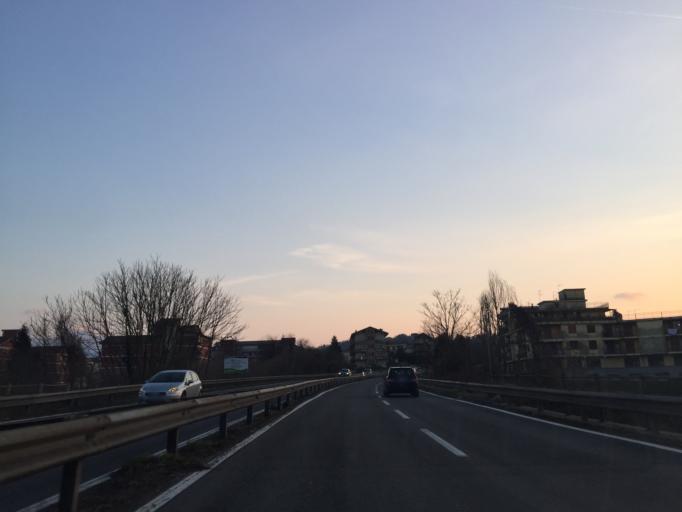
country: IT
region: Campania
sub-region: Provincia di Avellino
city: Atripalda
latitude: 40.9172
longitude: 14.8258
